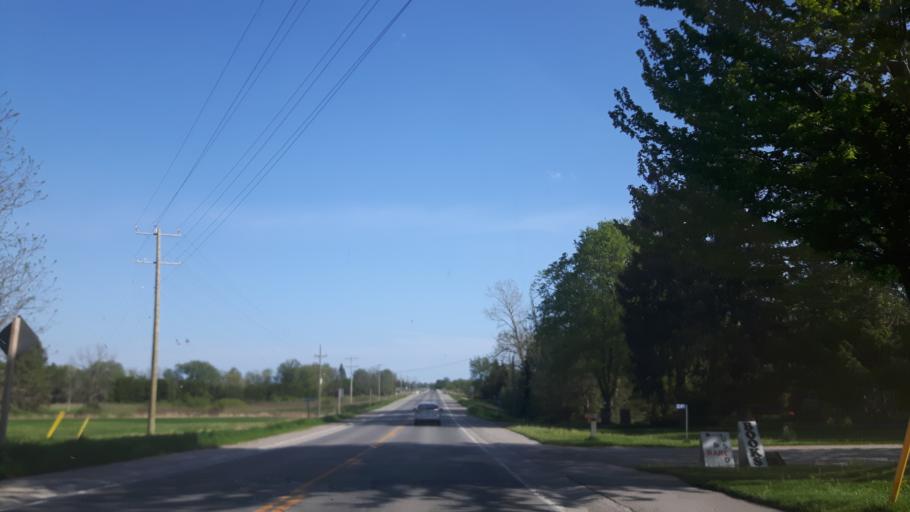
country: CA
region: Ontario
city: London
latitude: 43.1199
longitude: -81.3310
